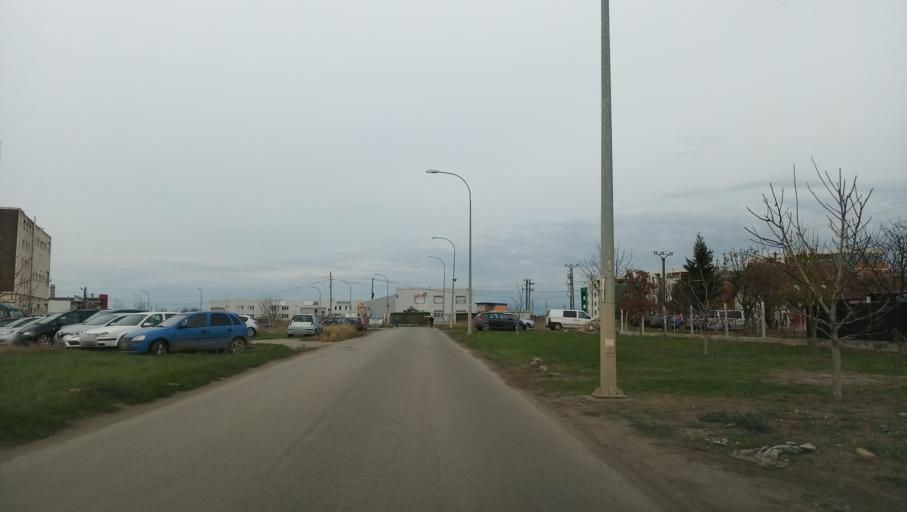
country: RO
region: Timis
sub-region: Comuna Ghiroda
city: Ghiroda
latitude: 45.7298
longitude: 21.2701
